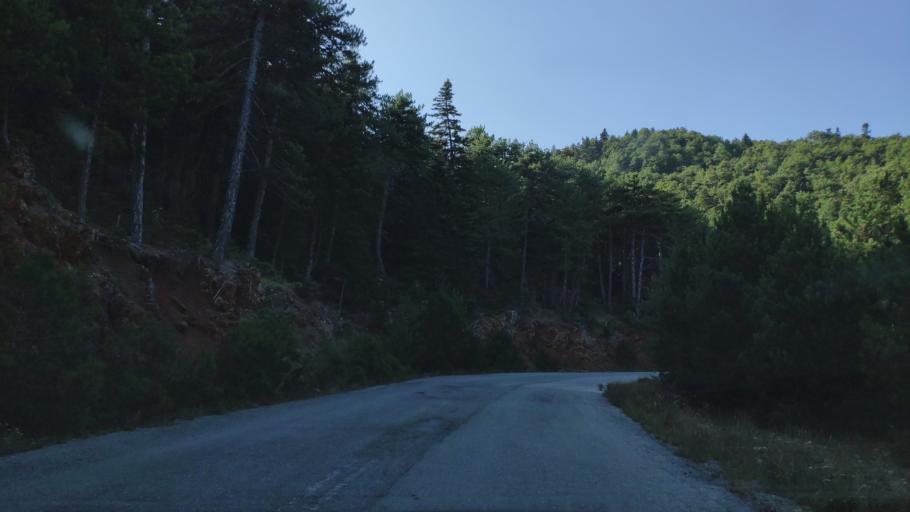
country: GR
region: West Greece
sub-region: Nomos Achaias
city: Aiyira
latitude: 38.0189
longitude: 22.4041
